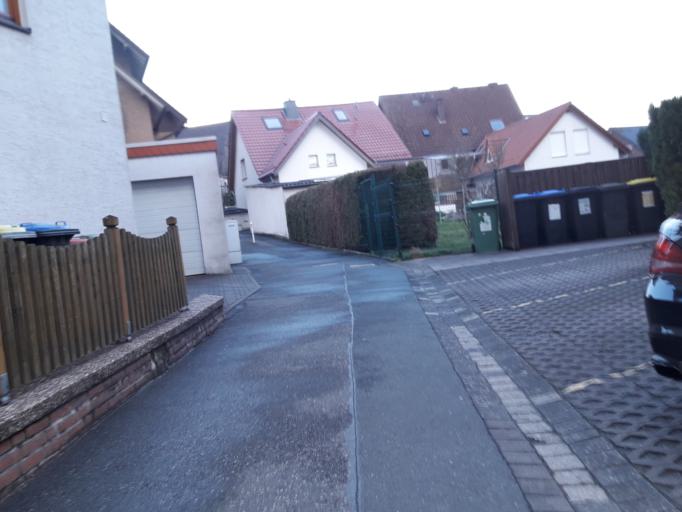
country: DE
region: North Rhine-Westphalia
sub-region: Regierungsbezirk Detmold
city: Paderborn
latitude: 51.6890
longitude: 8.6937
